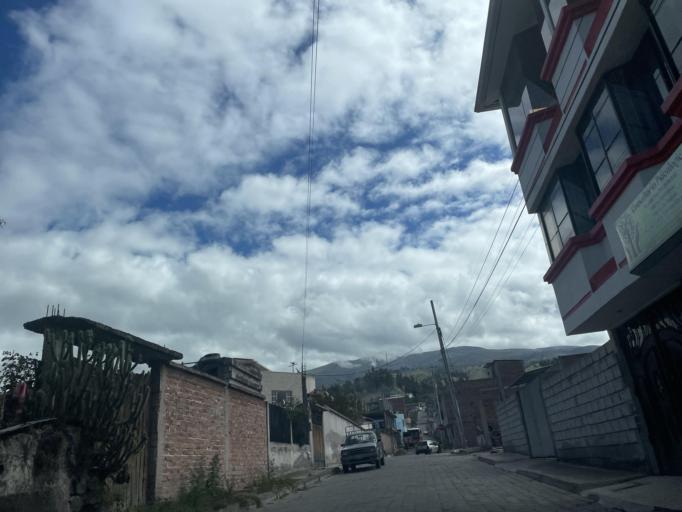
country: EC
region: Chimborazo
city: Guano
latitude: -1.6073
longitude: -78.6405
